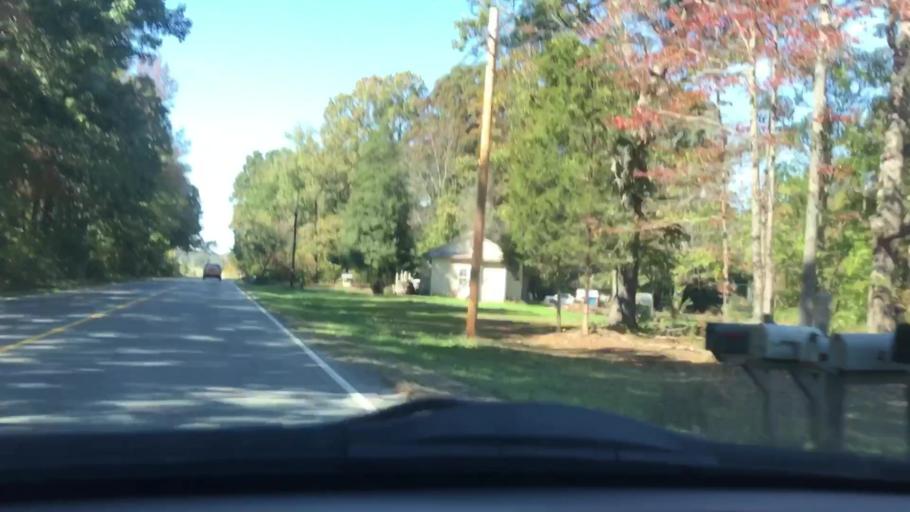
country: US
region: North Carolina
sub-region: Randolph County
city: Randleman
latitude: 35.8167
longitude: -79.8440
